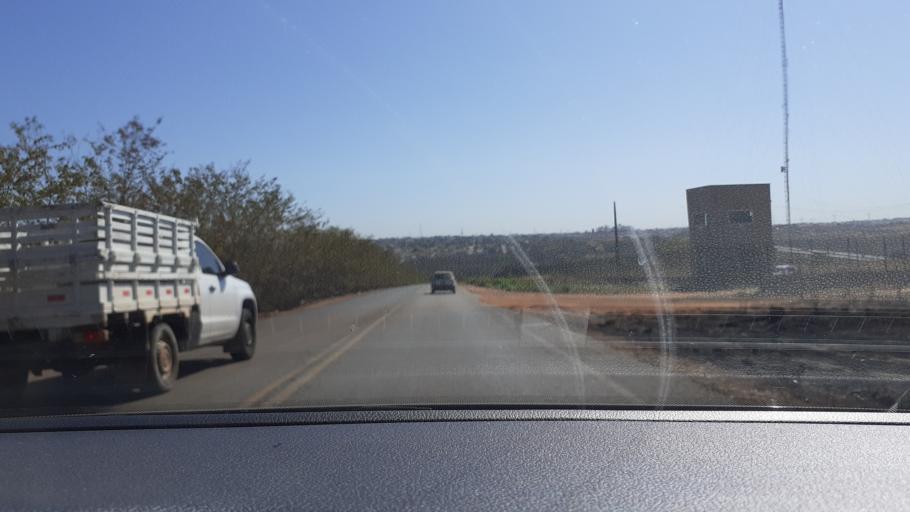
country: BR
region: Goias
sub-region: Aparecida De Goiania
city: Aparecida de Goiania
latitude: -16.8567
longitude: -49.2559
